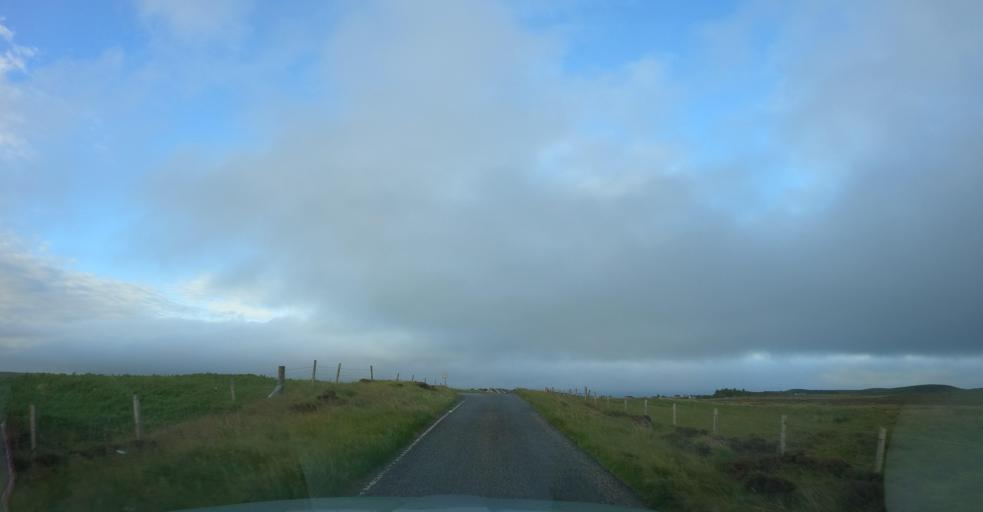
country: GB
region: Scotland
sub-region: Eilean Siar
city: Stornoway
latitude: 58.2027
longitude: -6.2372
